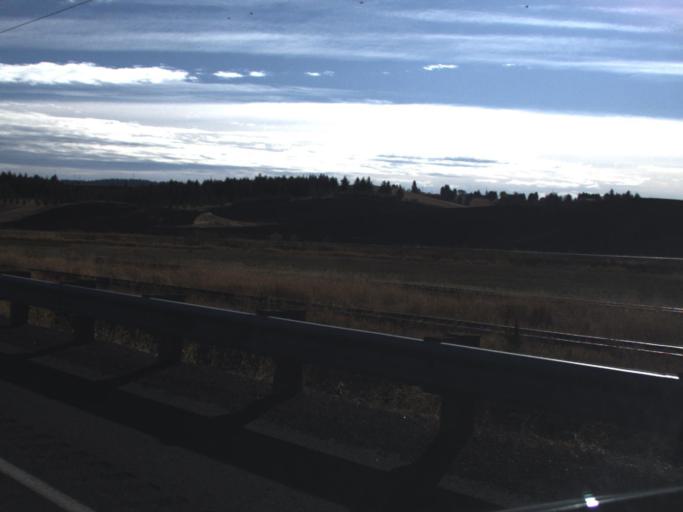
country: US
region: Idaho
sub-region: Latah County
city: Moscow
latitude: 46.7329
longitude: -117.0443
